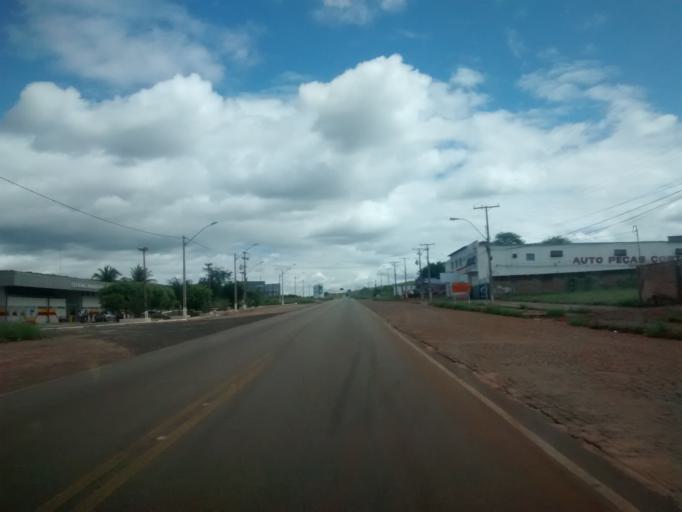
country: BR
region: Bahia
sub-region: Brumado
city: Brumado
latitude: -14.2188
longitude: -41.6866
